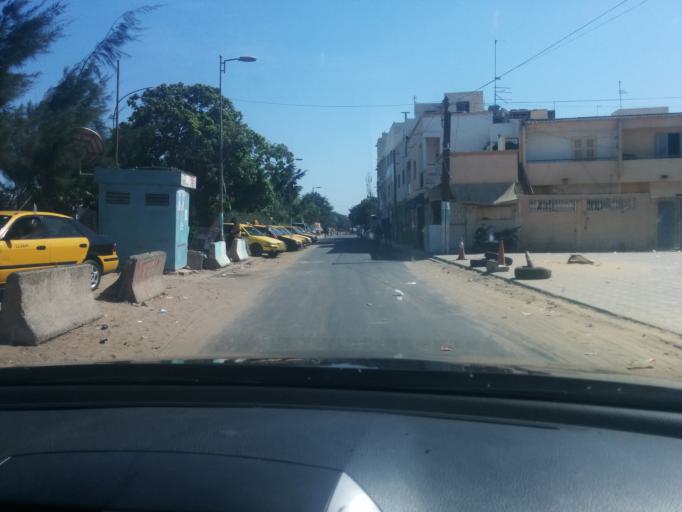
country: SN
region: Dakar
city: Grand Dakar
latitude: 14.7429
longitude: -17.4447
